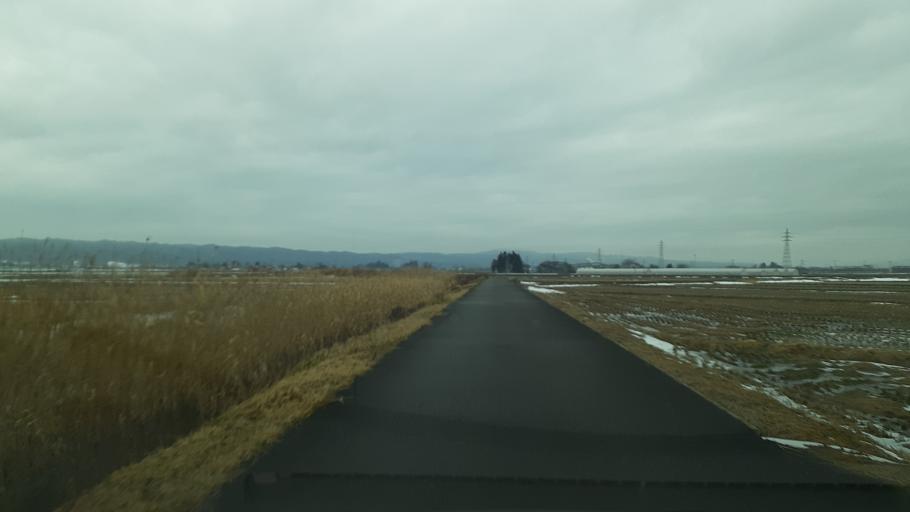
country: JP
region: Fukushima
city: Kitakata
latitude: 37.5410
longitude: 139.8409
